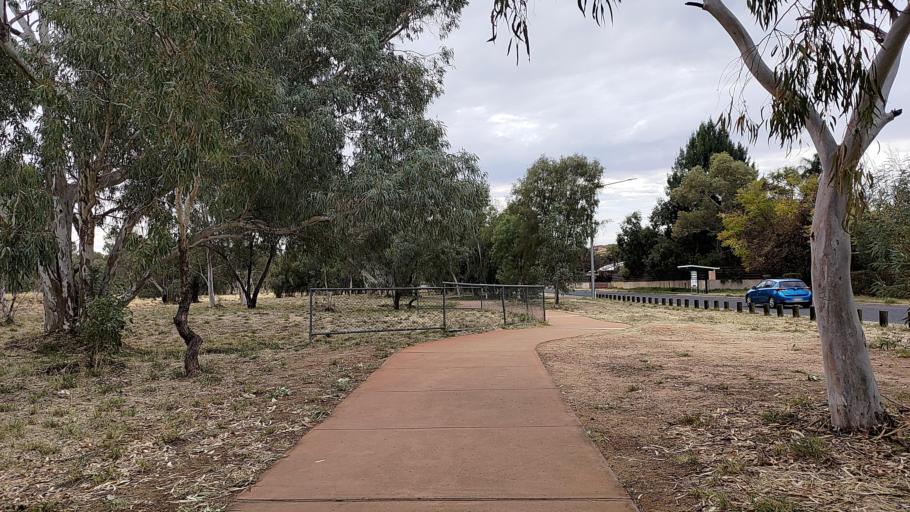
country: AU
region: Northern Territory
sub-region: Alice Springs
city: Alice Springs
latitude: -23.7095
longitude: 133.8809
